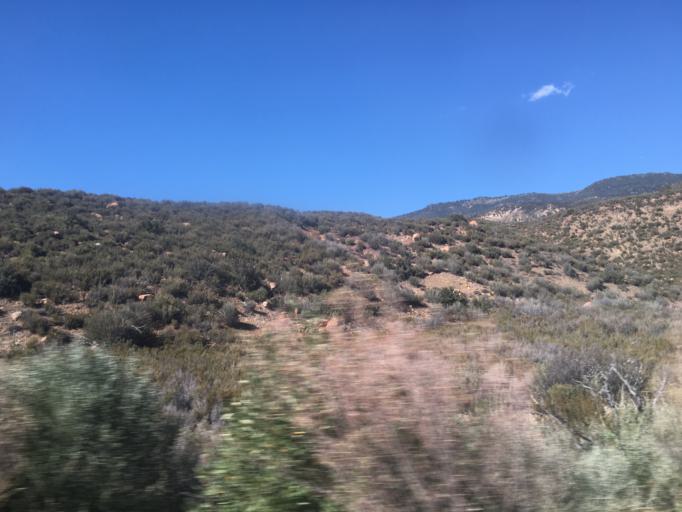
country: US
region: California
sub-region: Ventura County
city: Meiners Oaks
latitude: 34.5946
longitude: -119.3043
